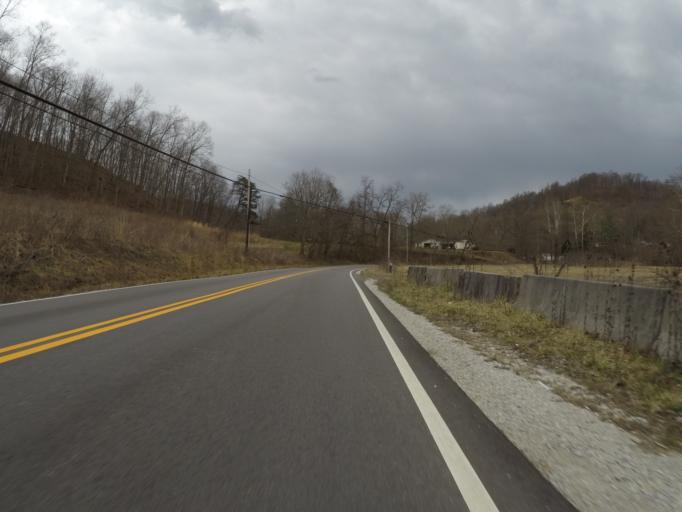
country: US
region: Ohio
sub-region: Lawrence County
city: Burlington
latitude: 38.4340
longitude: -82.4934
